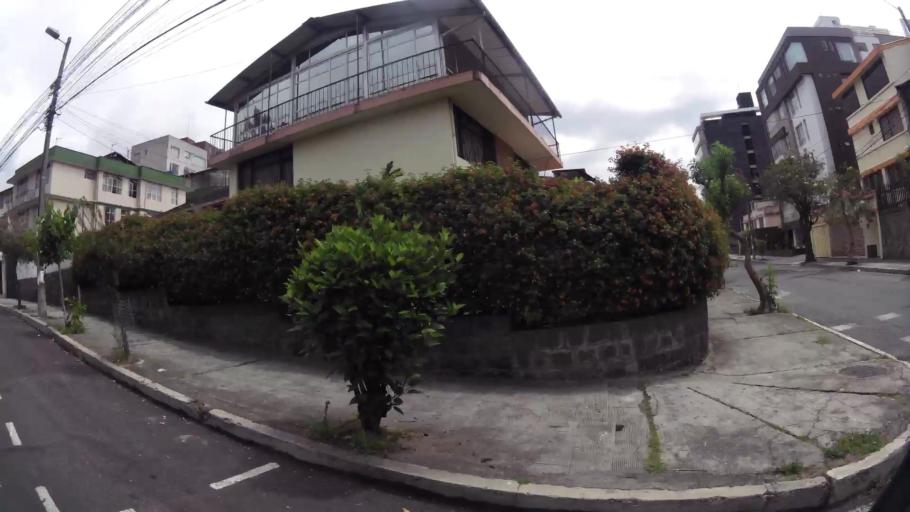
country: EC
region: Pichincha
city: Quito
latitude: -0.1806
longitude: -78.4925
